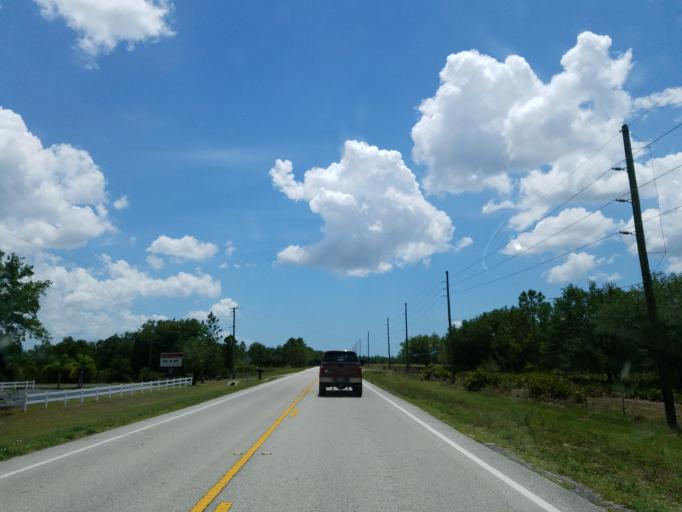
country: US
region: Florida
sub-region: Charlotte County
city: Harbour Heights
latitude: 27.0683
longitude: -82.0221
